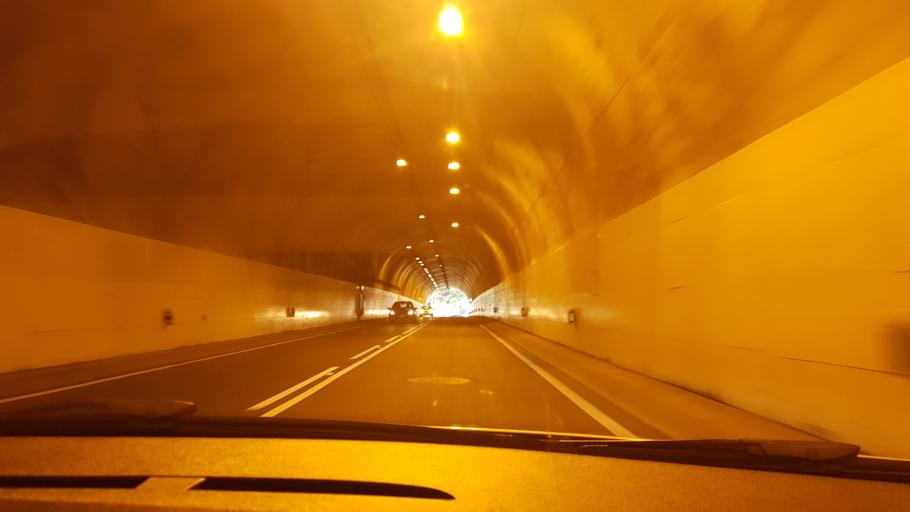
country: PT
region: Madeira
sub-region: Santana
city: Santana
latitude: 32.8095
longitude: -16.8774
